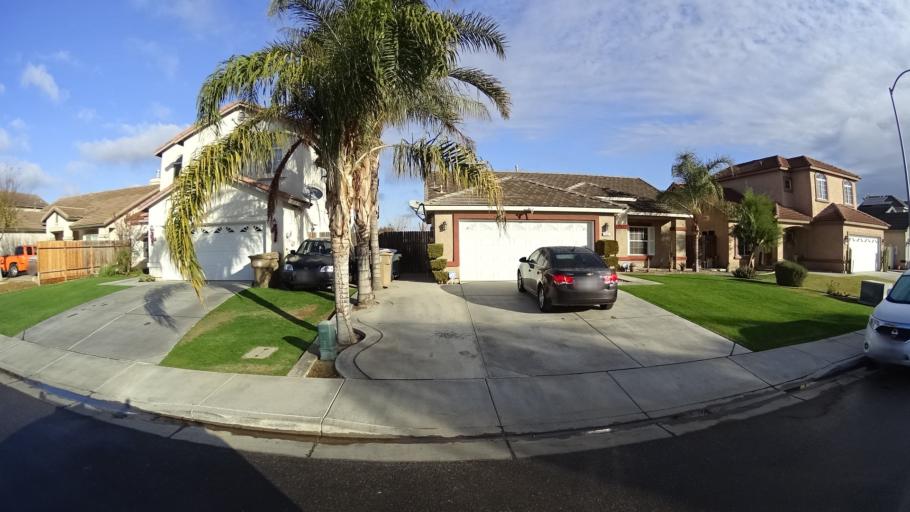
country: US
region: California
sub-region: Kern County
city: Greenfield
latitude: 35.2915
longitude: -118.9982
